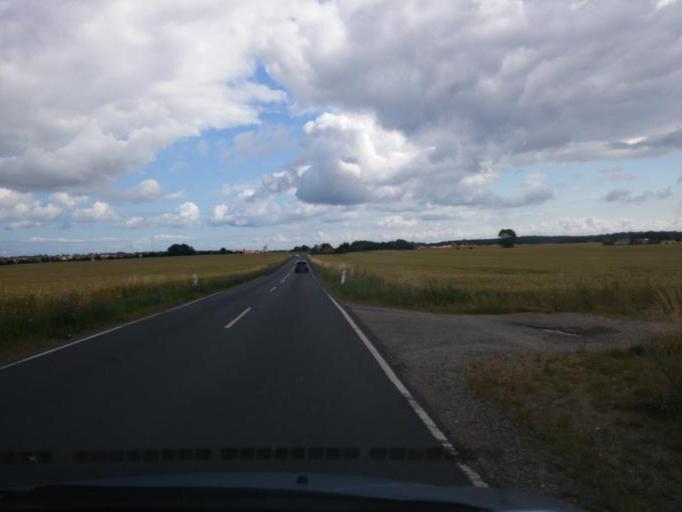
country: DK
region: South Denmark
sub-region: Kerteminde Kommune
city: Kerteminde
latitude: 55.4346
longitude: 10.6309
